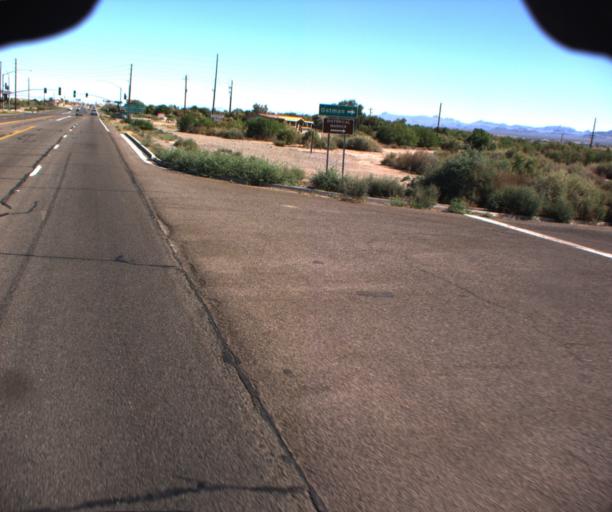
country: US
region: Arizona
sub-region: Mohave County
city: Mohave Valley
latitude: 34.9663
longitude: -114.5979
